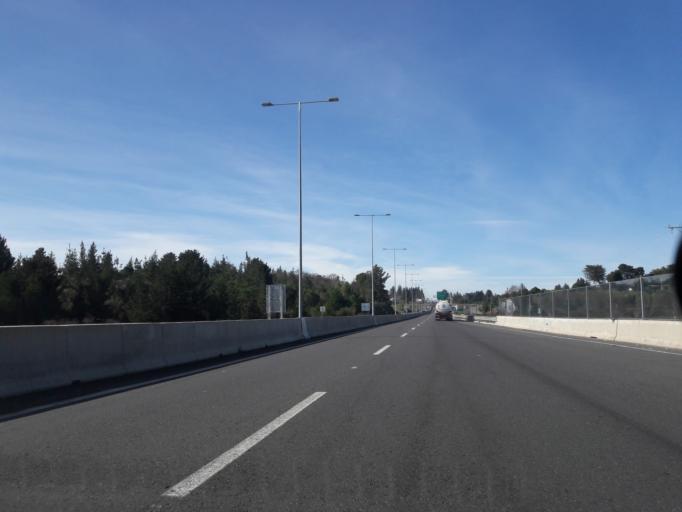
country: CL
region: Biobio
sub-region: Provincia de Biobio
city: Yumbel
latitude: -36.9607
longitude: -72.7263
